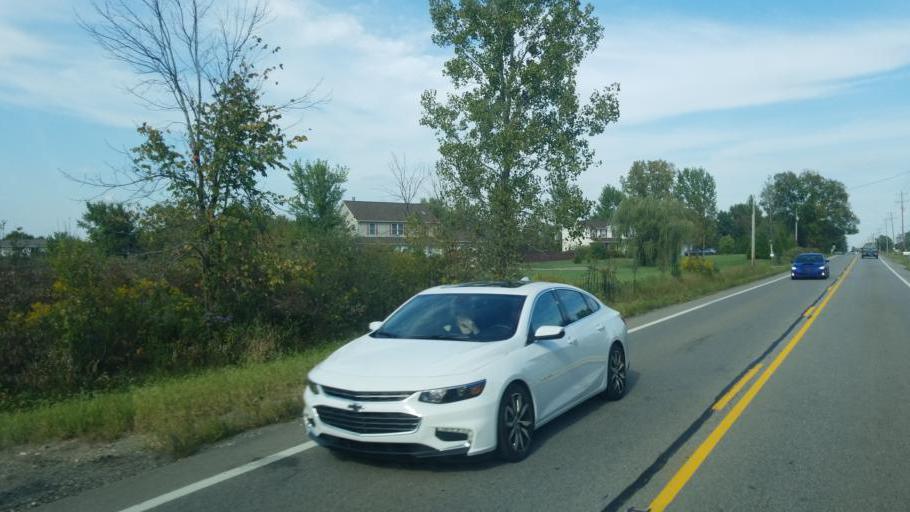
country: US
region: Ohio
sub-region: Licking County
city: Johnstown
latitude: 40.1282
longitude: -82.7432
